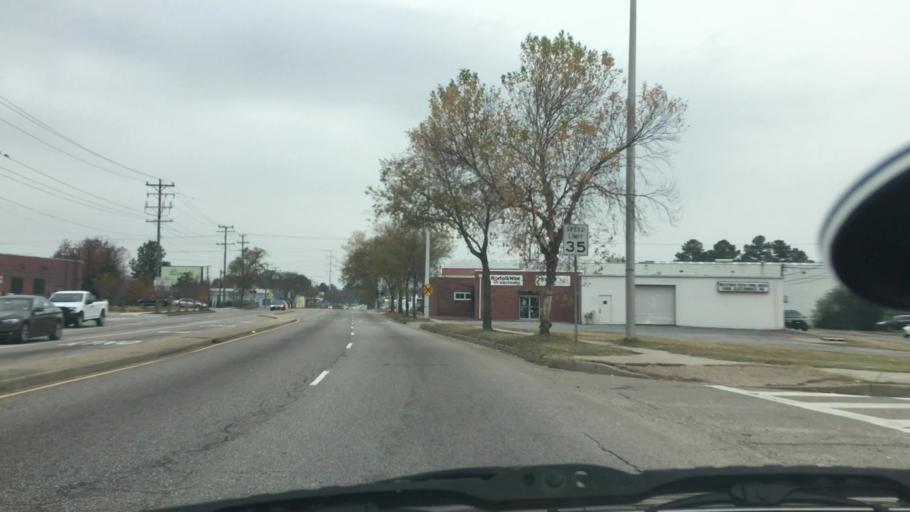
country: US
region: Virginia
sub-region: City of Norfolk
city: Norfolk
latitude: 36.8635
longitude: -76.2443
